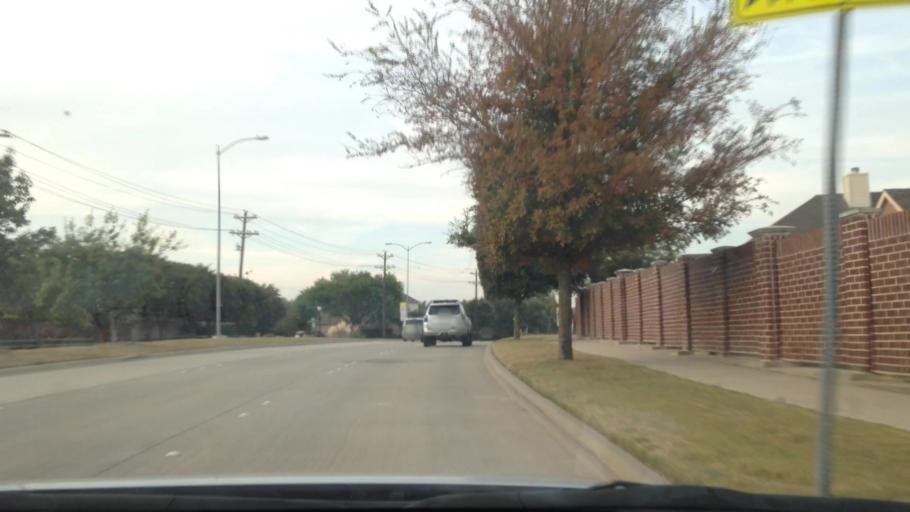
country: US
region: Texas
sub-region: Collin County
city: Frisco
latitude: 33.1101
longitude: -96.7572
